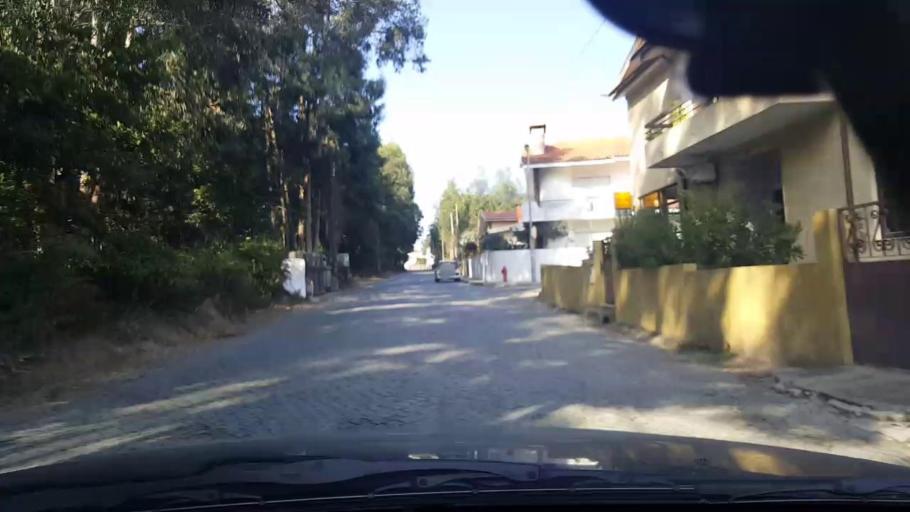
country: PT
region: Porto
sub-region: Maia
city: Gemunde
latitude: 41.2677
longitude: -8.6817
